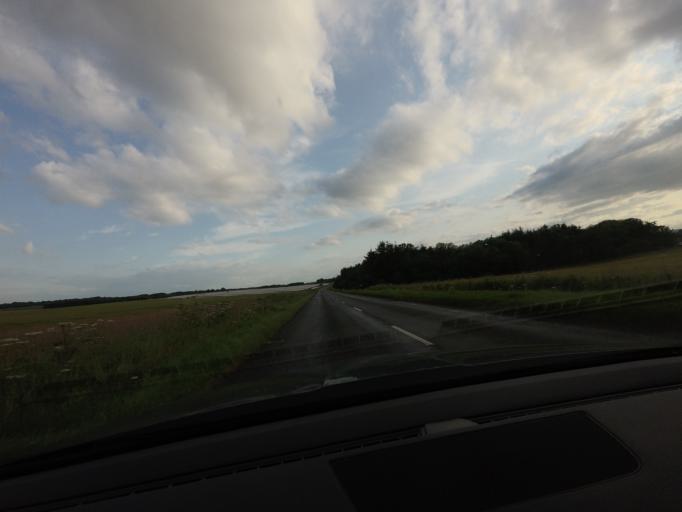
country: GB
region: Scotland
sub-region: Aberdeenshire
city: Turriff
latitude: 57.5564
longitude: -2.4382
